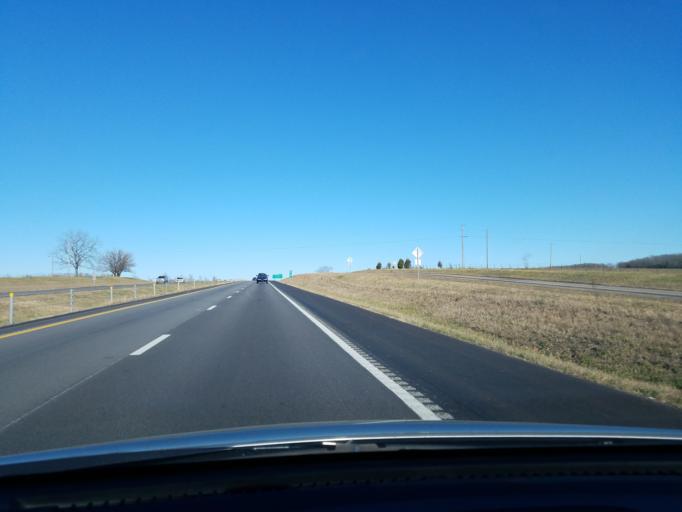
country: US
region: Missouri
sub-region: Webster County
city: Marshfield
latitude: 37.4134
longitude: -92.8880
